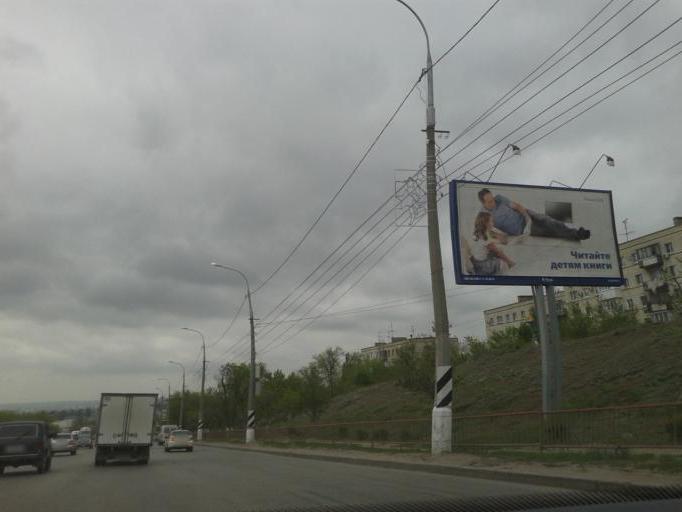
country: RU
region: Volgograd
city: Volgograd
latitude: 48.6681
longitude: 44.4413
